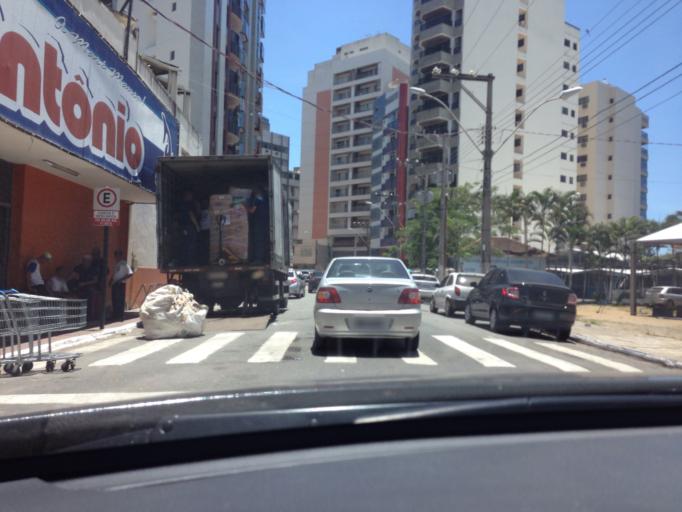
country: BR
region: Espirito Santo
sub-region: Guarapari
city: Guarapari
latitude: -20.6738
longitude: -40.4997
